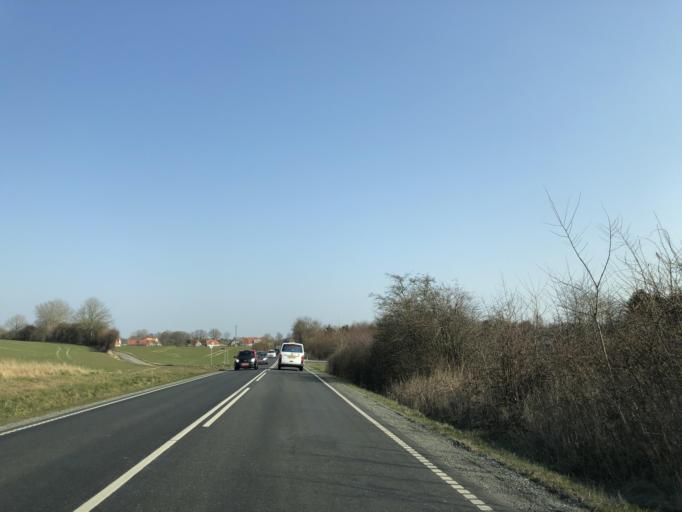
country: DK
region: South Denmark
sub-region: Sonderborg Kommune
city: Nordborg
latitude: 55.0256
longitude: 9.7806
